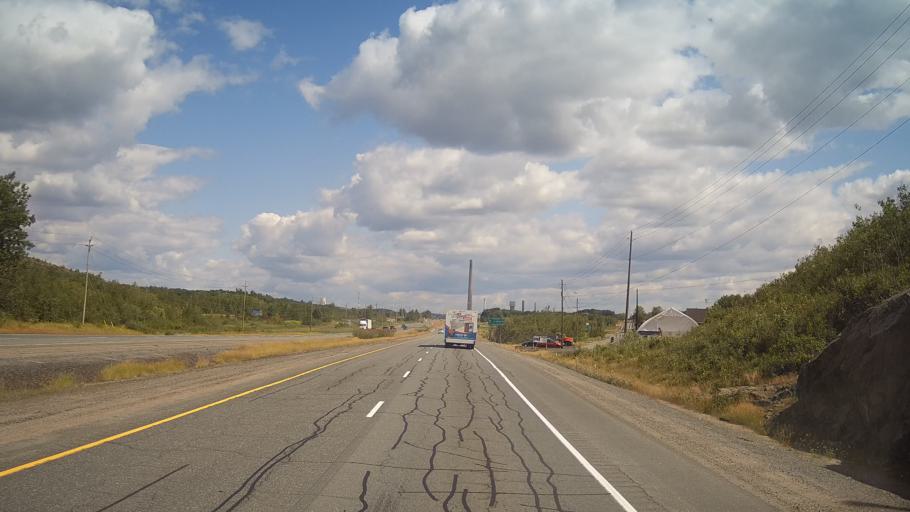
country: CA
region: Ontario
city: Greater Sudbury
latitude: 46.4449
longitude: -81.1000
